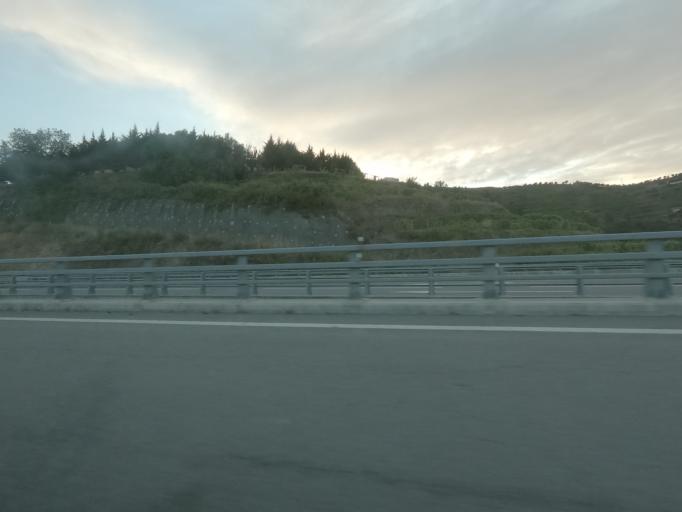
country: PT
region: Vila Real
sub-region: Peso da Regua
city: Peso da Regua
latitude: 41.1722
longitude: -7.7685
